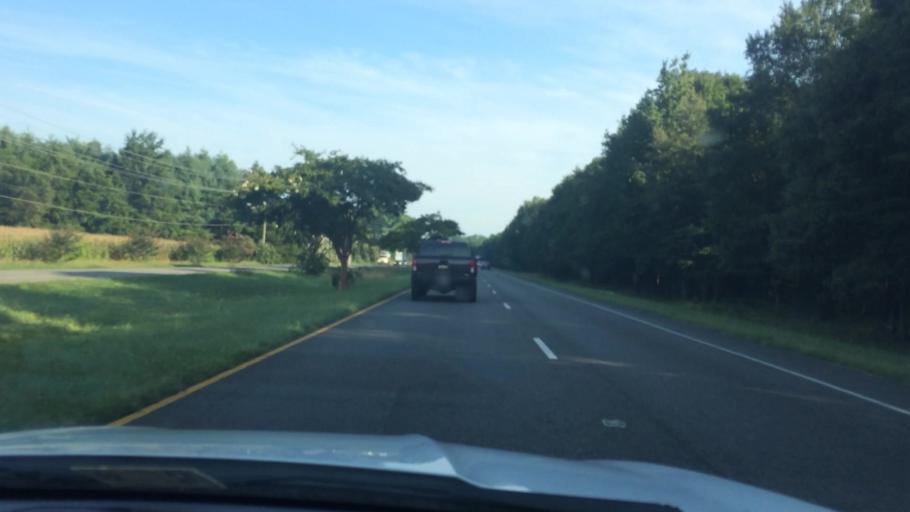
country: US
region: Virginia
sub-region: Gloucester County
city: Gloucester Courthouse
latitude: 37.3618
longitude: -76.5251
